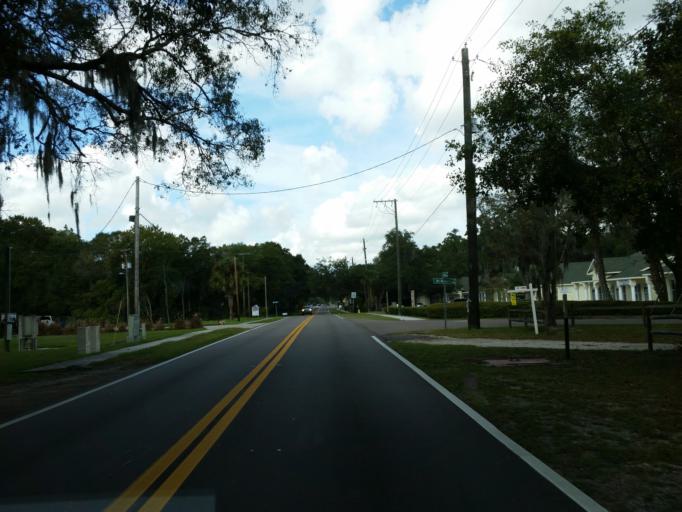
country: US
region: Florida
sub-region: Hillsborough County
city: Riverview
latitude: 27.8622
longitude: -82.3224
